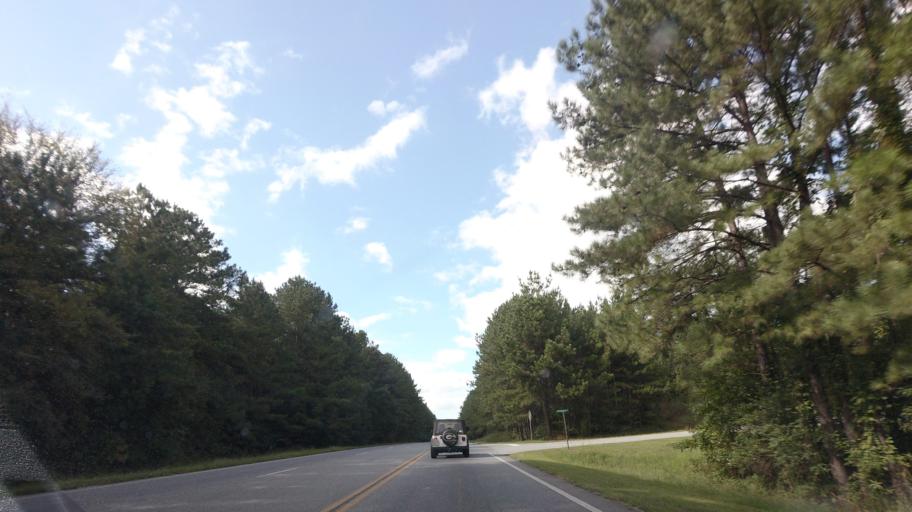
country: US
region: Georgia
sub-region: Bibb County
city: Macon
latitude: 32.9845
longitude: -83.7324
